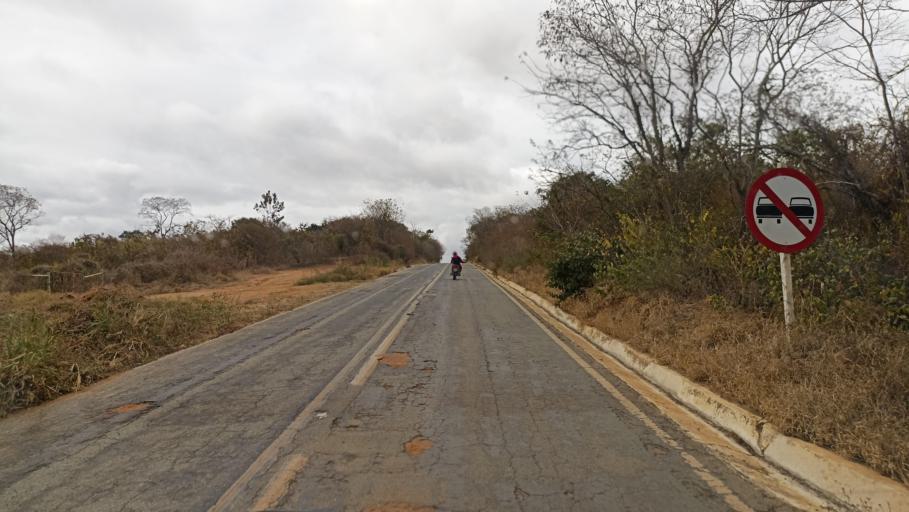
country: BR
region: Minas Gerais
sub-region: Itinga
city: Itinga
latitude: -16.6338
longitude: -41.8005
